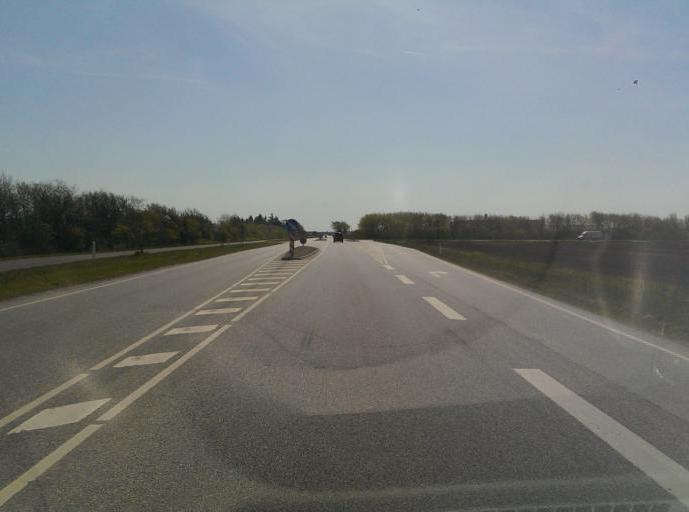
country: DK
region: South Denmark
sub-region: Esbjerg Kommune
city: Ribe
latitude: 55.3632
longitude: 8.7703
